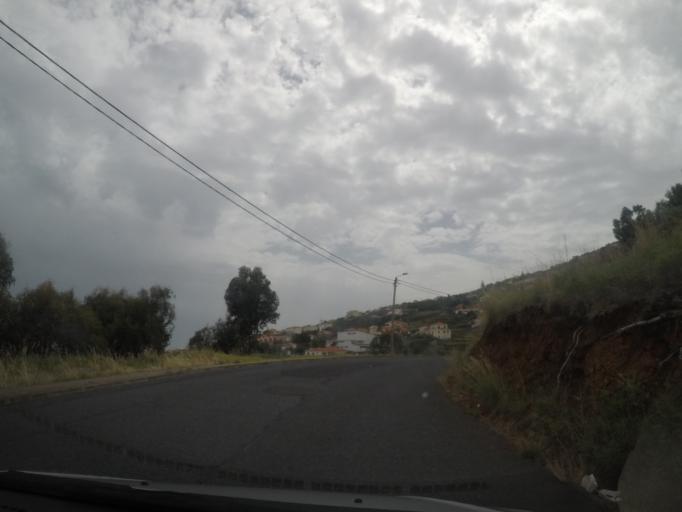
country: PT
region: Madeira
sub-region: Santa Cruz
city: Santa Cruz
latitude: 32.6765
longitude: -16.8097
